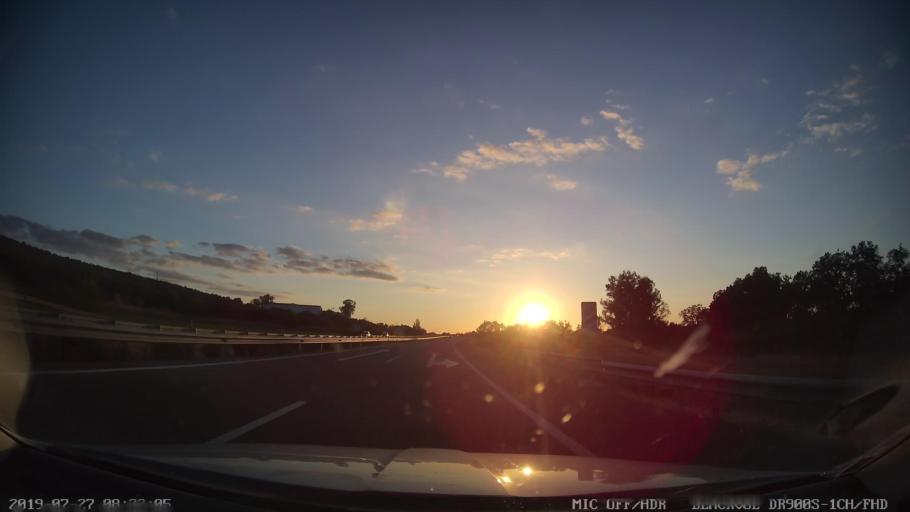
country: ES
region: Extremadura
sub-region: Provincia de Badajoz
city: Torremayor
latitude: 38.8602
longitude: -6.5377
